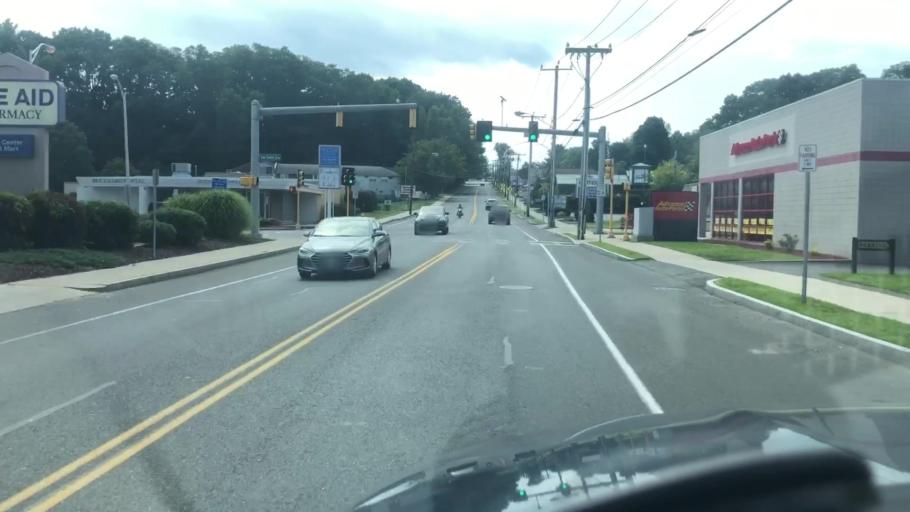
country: US
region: Massachusetts
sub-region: Hampden County
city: West Springfield
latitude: 42.1064
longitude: -72.6250
